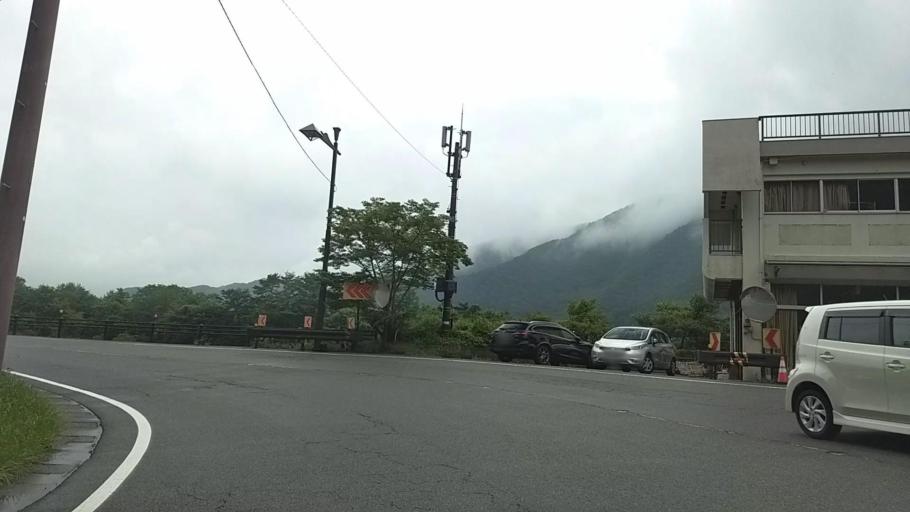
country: JP
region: Yamanashi
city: Fujikawaguchiko
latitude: 35.4894
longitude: 138.6113
